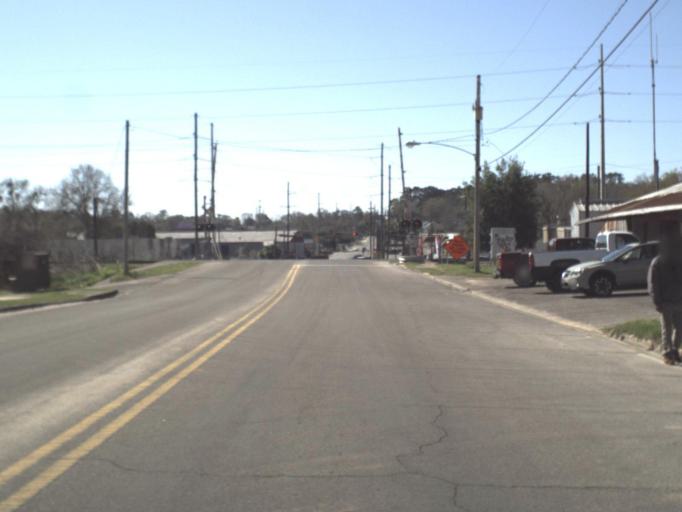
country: US
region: Florida
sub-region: Leon County
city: Tallahassee
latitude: 30.4335
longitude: -84.2820
